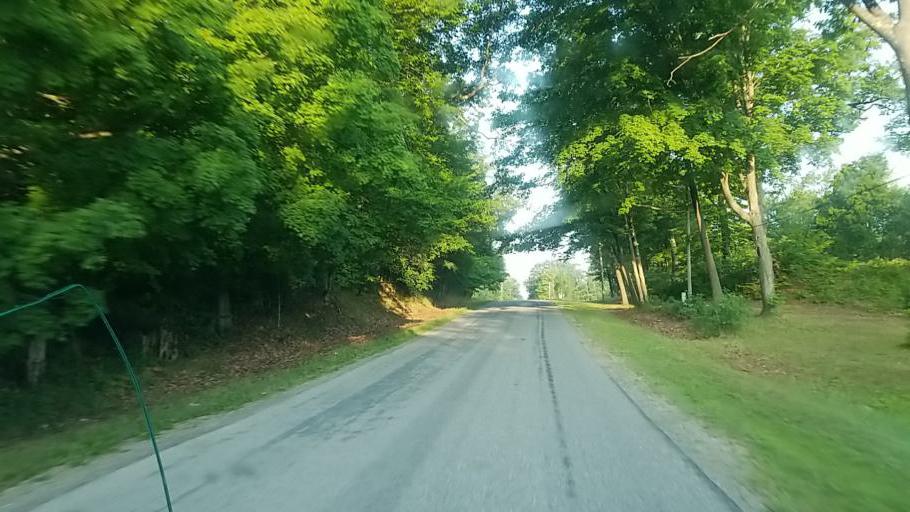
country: US
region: Michigan
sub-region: Muskegon County
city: Twin Lake
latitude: 43.4390
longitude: -86.0899
